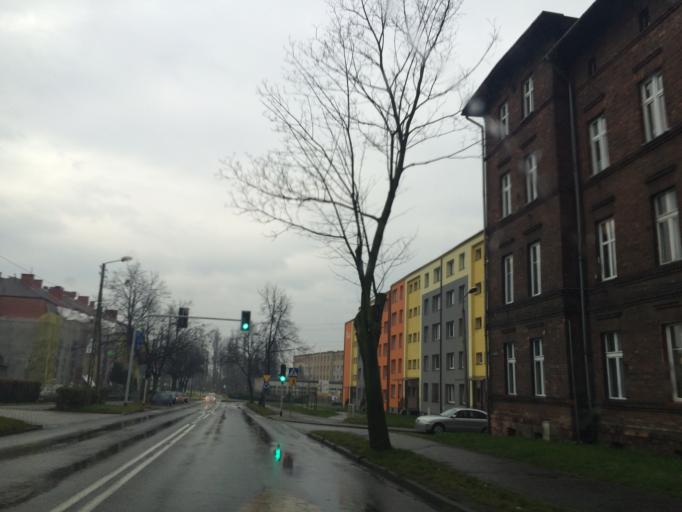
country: PL
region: Silesian Voivodeship
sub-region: Powiat tarnogorski
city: Radzionkow
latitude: 50.3864
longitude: 18.8994
